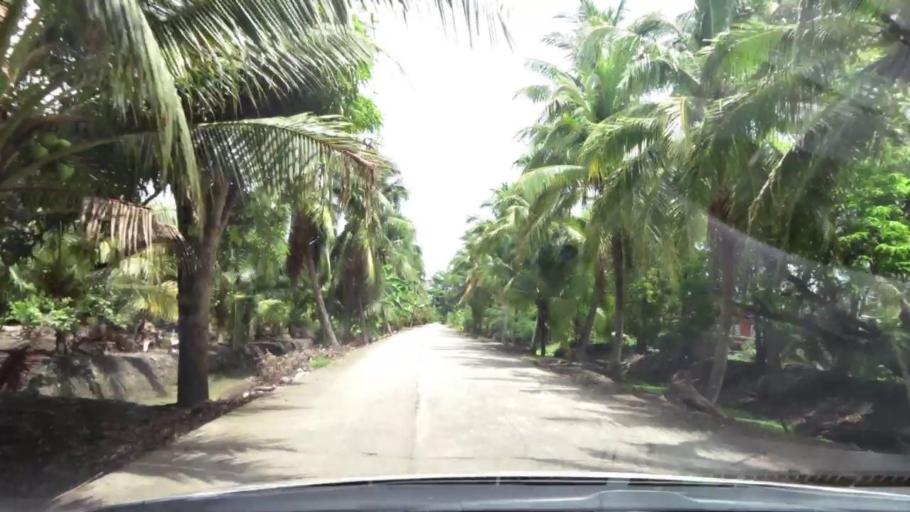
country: TH
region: Ratchaburi
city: Damnoen Saduak
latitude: 13.5249
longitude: 100.0044
